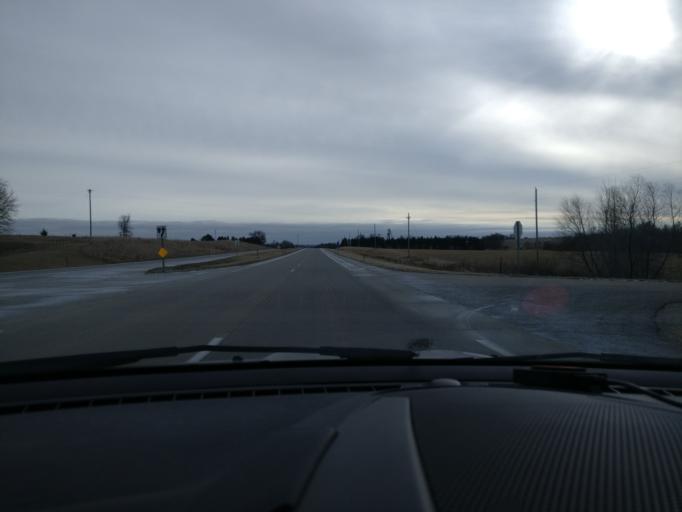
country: US
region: Nebraska
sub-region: Saunders County
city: Wahoo
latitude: 41.0749
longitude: -96.6404
